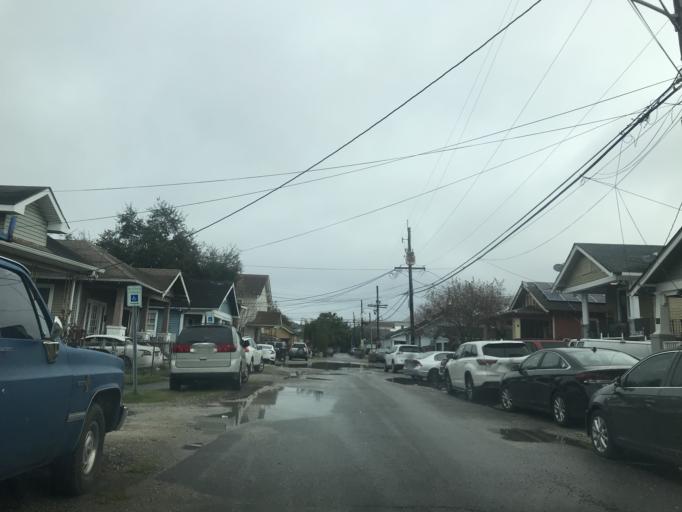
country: US
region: Louisiana
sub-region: Orleans Parish
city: New Orleans
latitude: 29.9709
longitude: -90.1065
